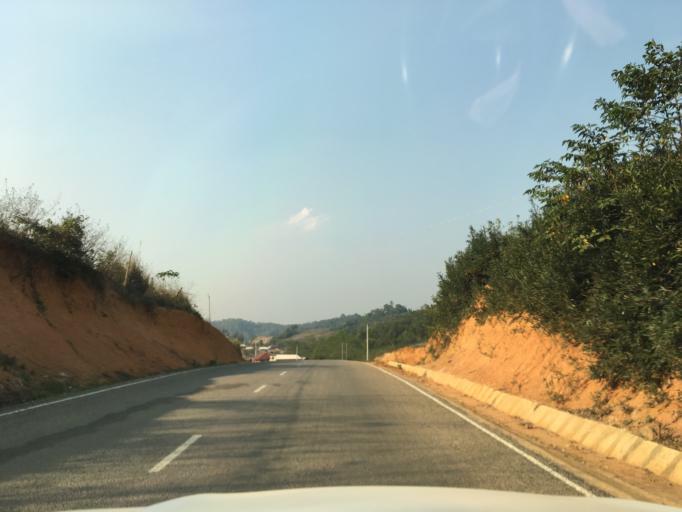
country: LA
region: Houaphan
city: Xam Nua
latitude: 20.5752
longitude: 104.0565
